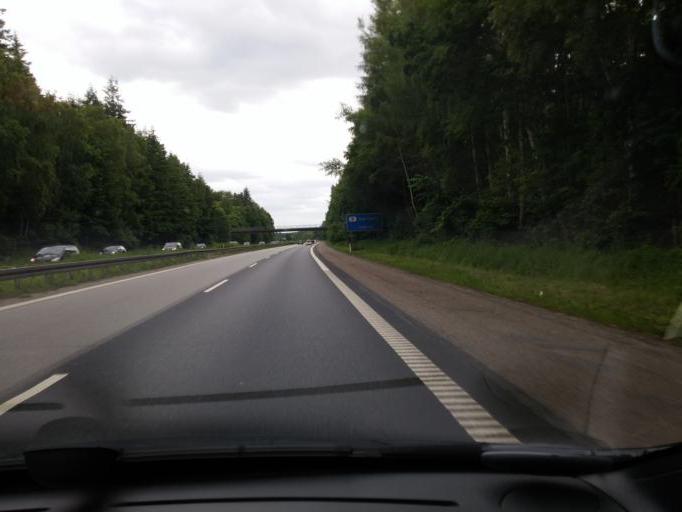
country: DK
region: Capital Region
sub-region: Fureso Kommune
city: Vaerlose
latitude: 55.7878
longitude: 12.3887
